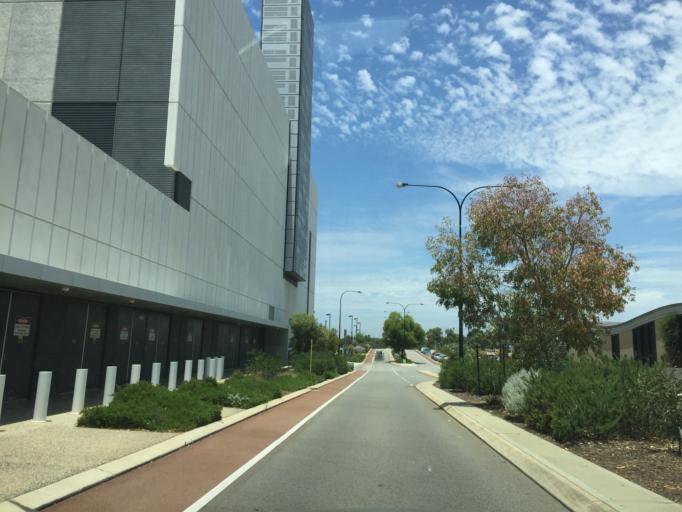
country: AU
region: Western Australia
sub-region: Melville
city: Winthrop
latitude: -32.0703
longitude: 115.8486
